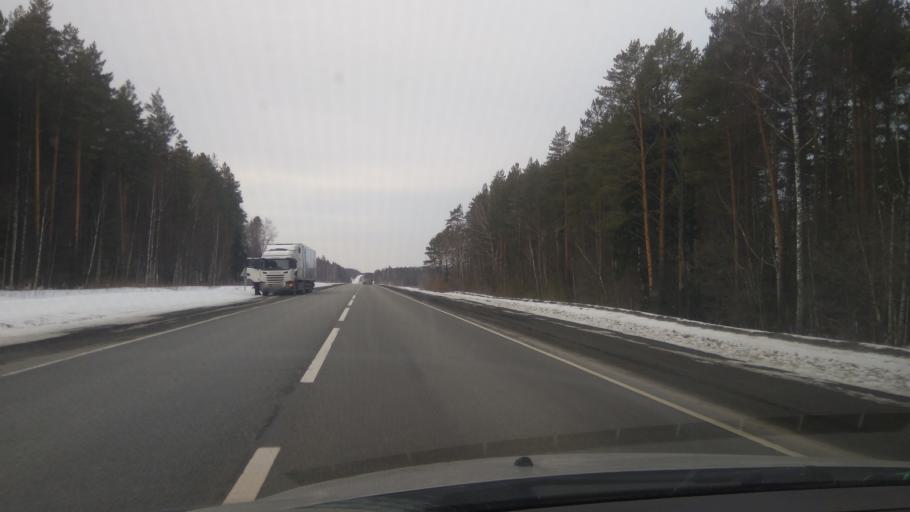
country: RU
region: Sverdlovsk
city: Bisert'
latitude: 56.8278
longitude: 58.7726
